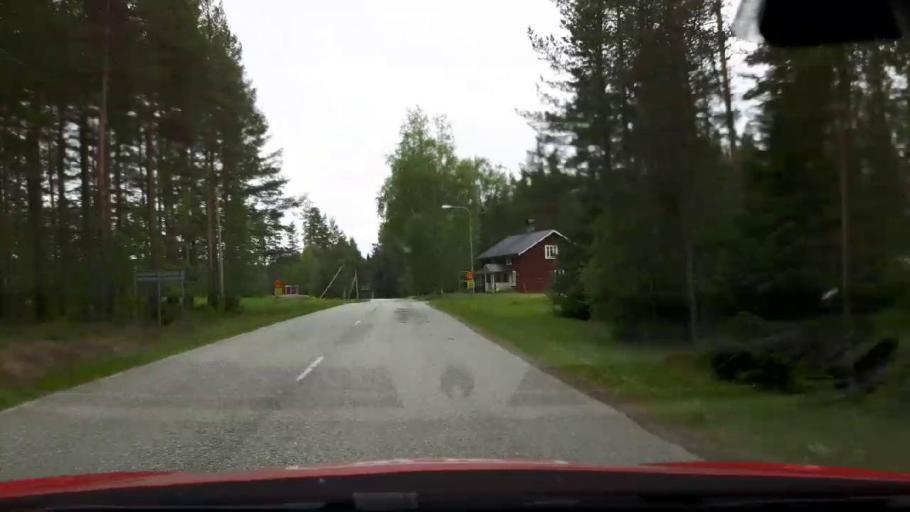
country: SE
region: Jaemtland
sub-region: Ragunda Kommun
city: Hammarstrand
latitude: 63.2205
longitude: 15.9361
